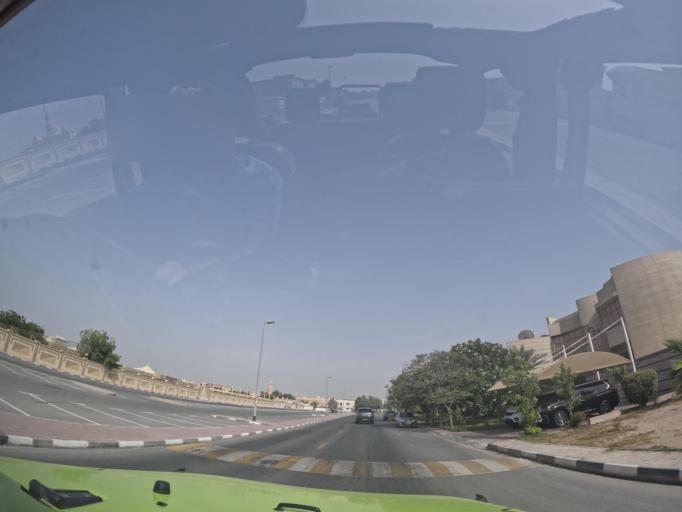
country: AE
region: Dubai
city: Dubai
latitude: 25.1461
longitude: 55.2151
